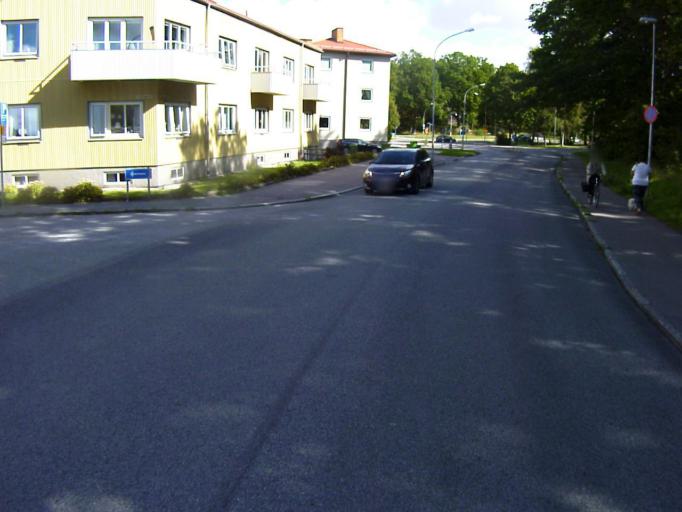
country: SE
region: Soedermanland
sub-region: Eskilstuna Kommun
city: Eskilstuna
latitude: 59.3651
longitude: 16.5337
